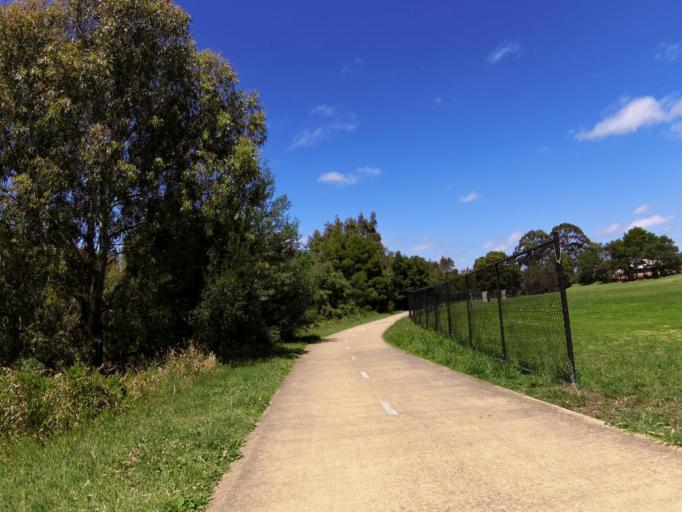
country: AU
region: Victoria
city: Brunswick East
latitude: -37.7729
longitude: 144.9859
